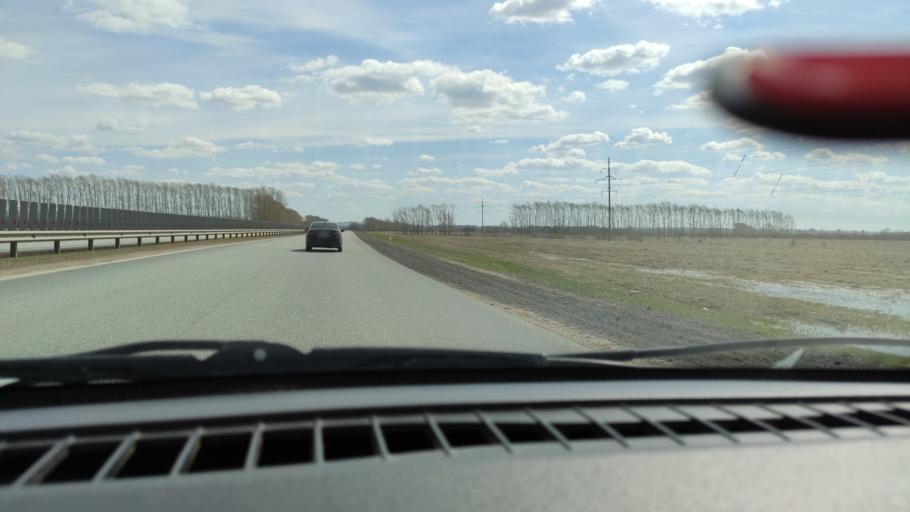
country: RU
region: Bashkortostan
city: Asanovo
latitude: 54.9936
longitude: 55.5089
